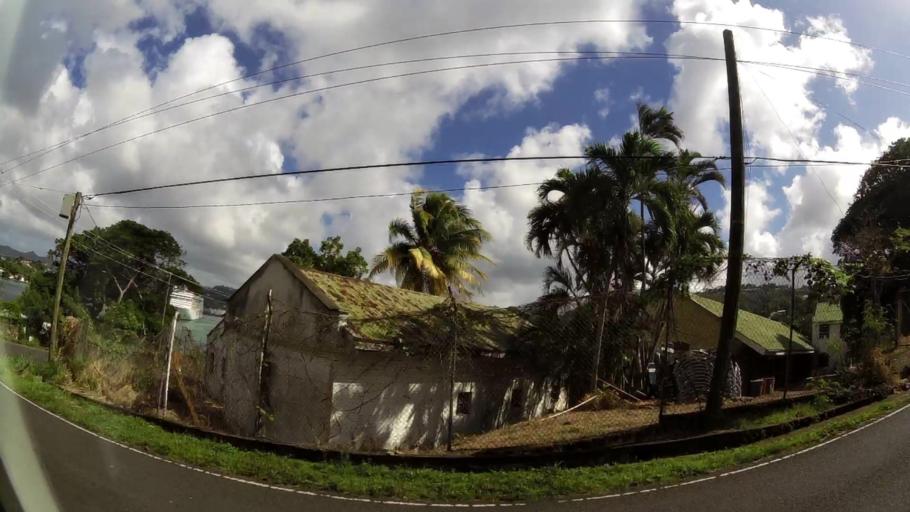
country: LC
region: Castries Quarter
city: Castries
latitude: 14.0132
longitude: -61.0030
